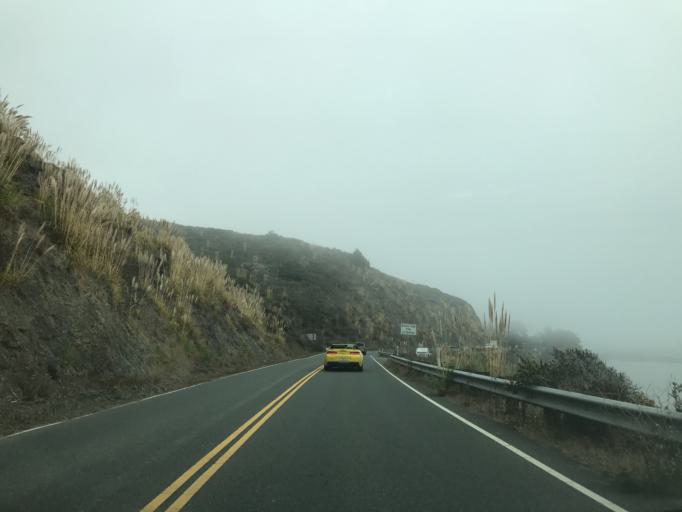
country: US
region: California
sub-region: Sonoma County
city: Monte Rio
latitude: 38.4532
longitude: -123.1302
